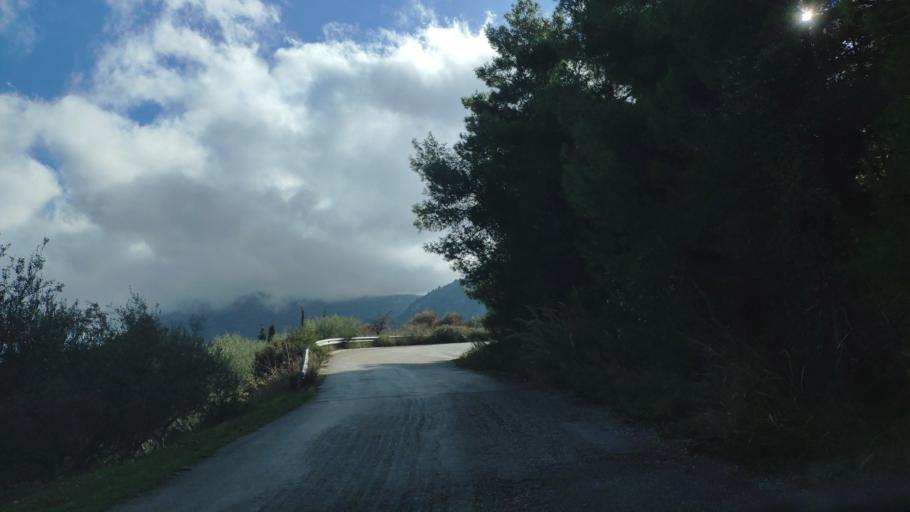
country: GR
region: West Greece
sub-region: Nomos Achaias
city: Aiyira
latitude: 38.1007
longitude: 22.4471
